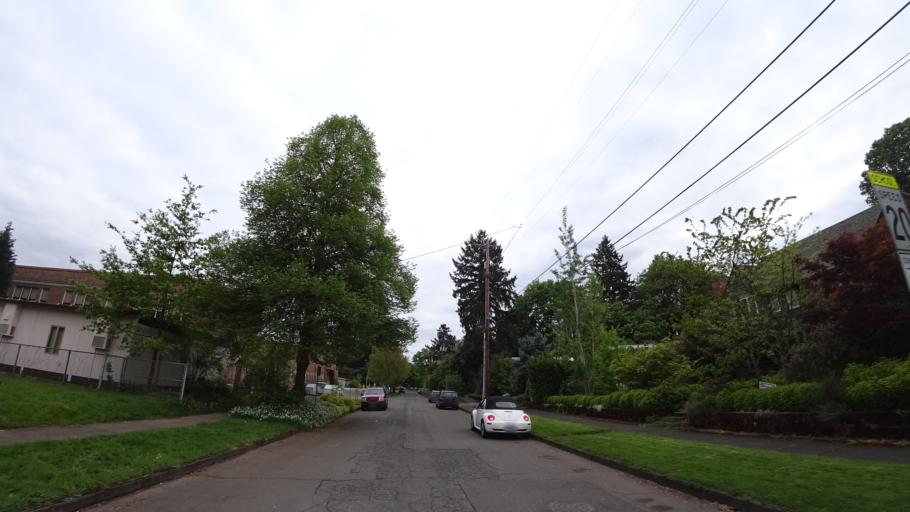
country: US
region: Oregon
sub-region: Clackamas County
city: Milwaukie
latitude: 45.4777
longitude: -122.6528
